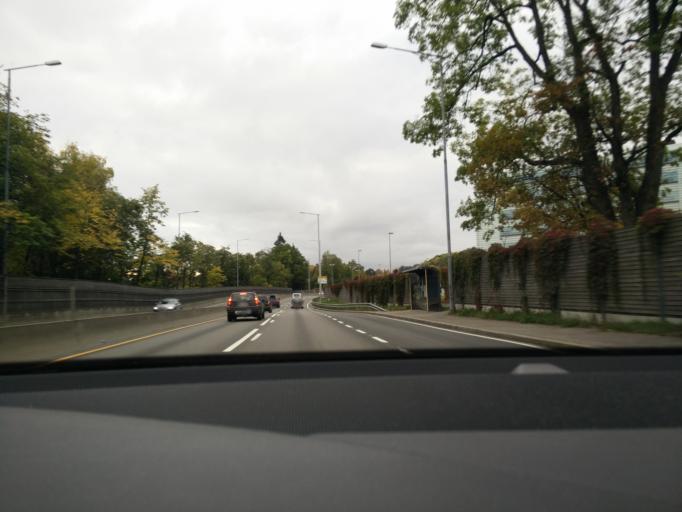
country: NO
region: Oslo
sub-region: Oslo
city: Sjolyststranda
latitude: 59.9309
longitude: 10.6662
